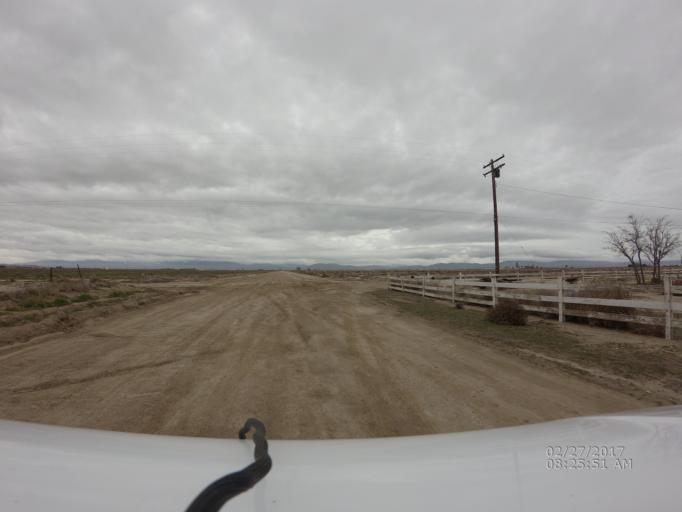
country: US
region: California
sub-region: Los Angeles County
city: Lancaster
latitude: 34.7121
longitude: -118.0144
